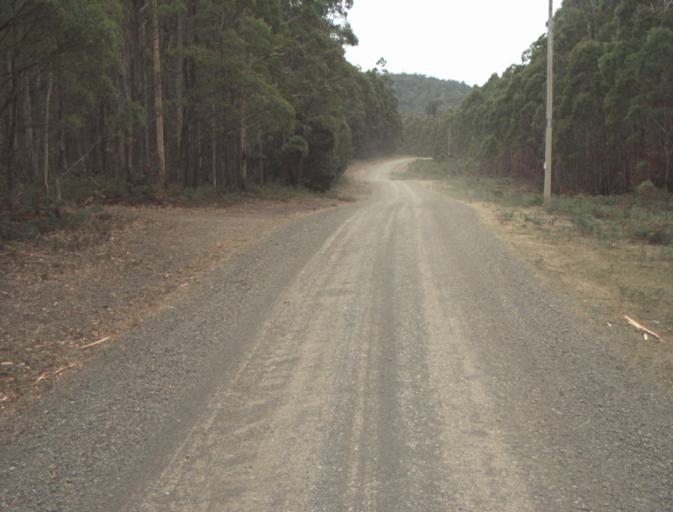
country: AU
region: Tasmania
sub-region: Dorset
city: Scottsdale
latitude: -41.4374
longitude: 147.5149
